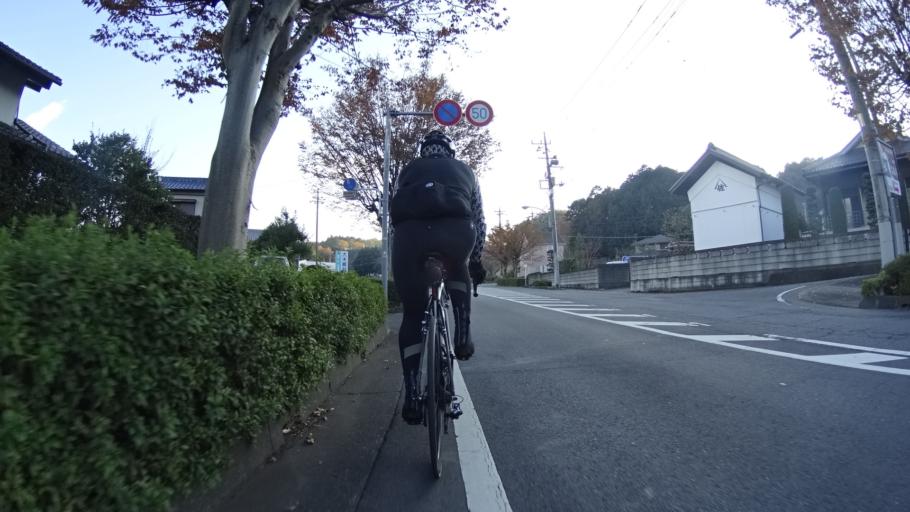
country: JP
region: Saitama
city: Hanno
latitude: 35.8467
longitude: 139.3146
